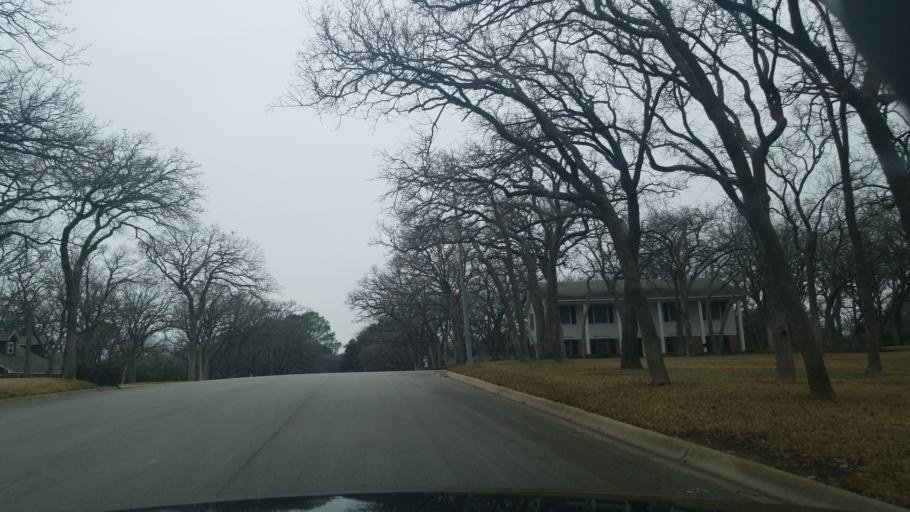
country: US
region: Texas
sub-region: Denton County
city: Denton
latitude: 33.1865
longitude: -97.1154
